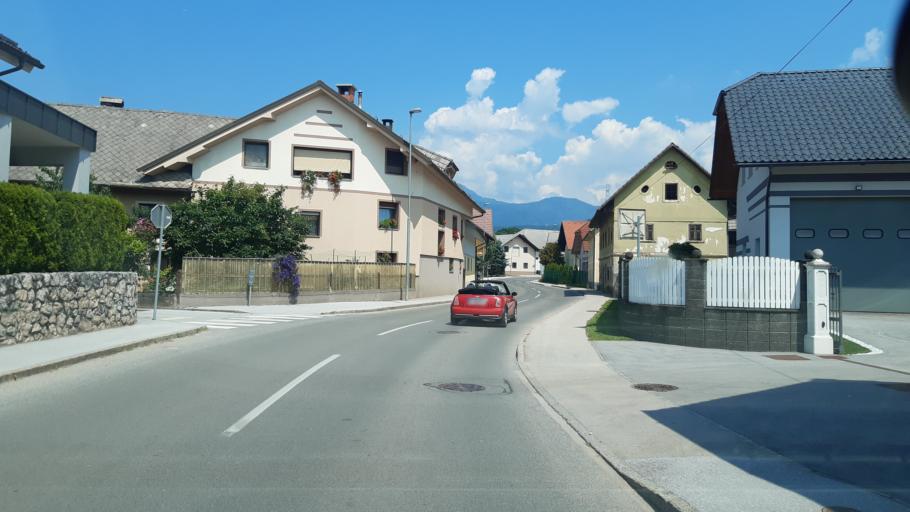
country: SI
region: Cerklje na Gorenjskem
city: Cerklje na Gorenjskem
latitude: 46.2395
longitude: 14.4848
